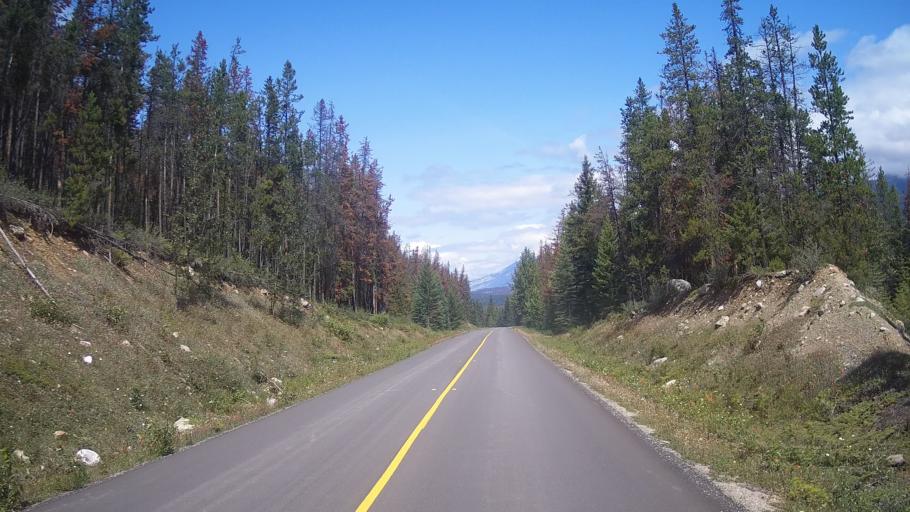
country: CA
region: Alberta
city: Jasper Park Lodge
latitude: 52.7827
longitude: -118.0325
